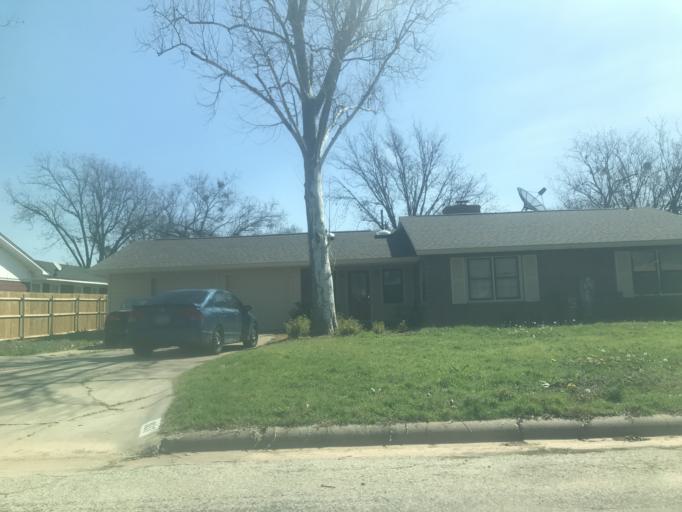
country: US
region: Texas
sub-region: Taylor County
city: Abilene
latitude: 32.4372
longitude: -99.7764
